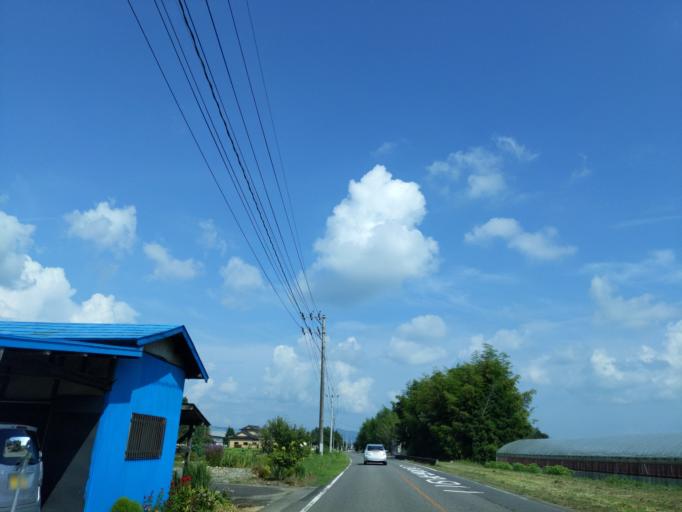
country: JP
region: Fukushima
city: Sukagawa
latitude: 37.3060
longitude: 140.3333
